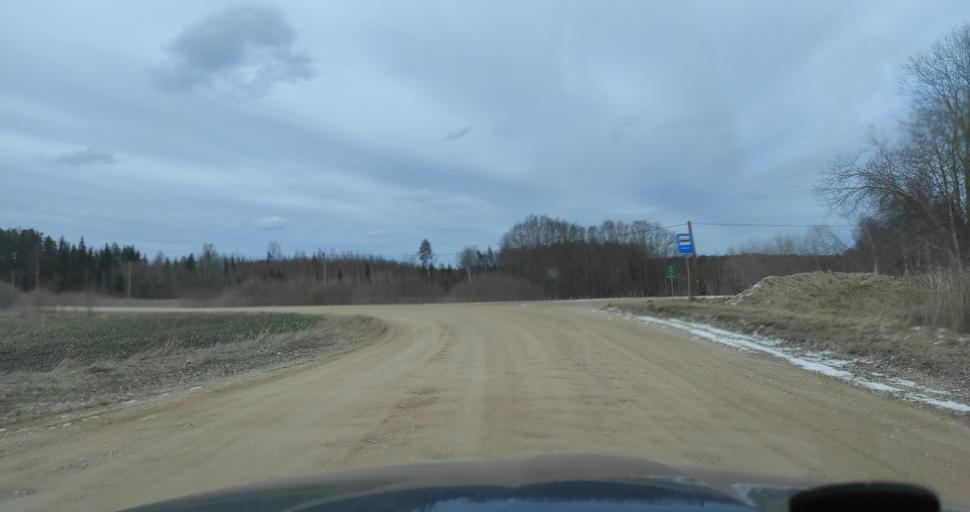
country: LV
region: Tukuma Rajons
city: Tukums
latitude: 57.0422
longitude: 23.0359
